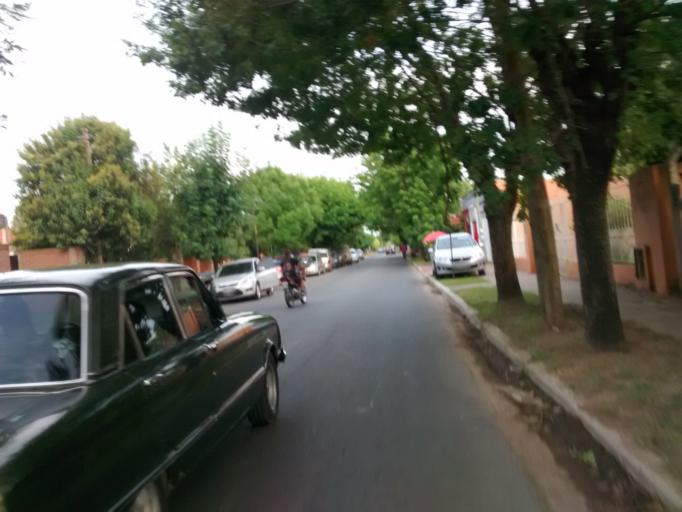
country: AR
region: Buenos Aires
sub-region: Partido de La Plata
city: La Plata
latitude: -34.8910
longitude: -58.0411
